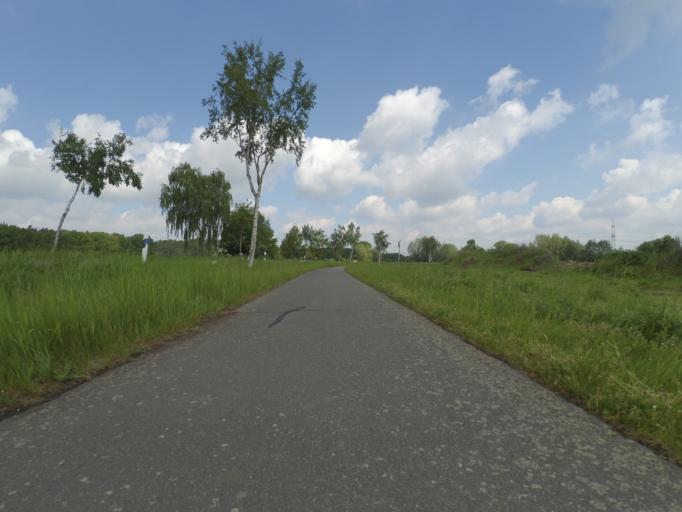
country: DE
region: Lower Saxony
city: Didderse
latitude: 52.3752
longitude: 10.3431
